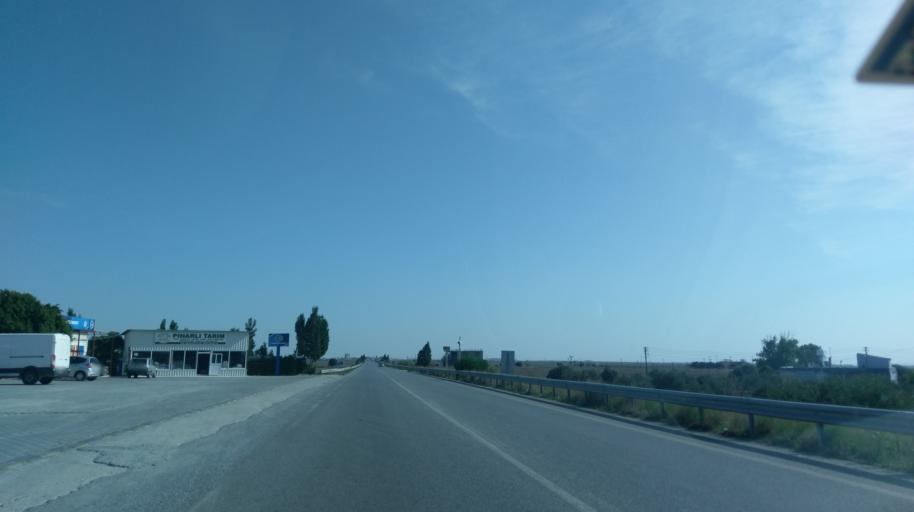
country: CY
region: Ammochostos
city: Lefkonoiko
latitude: 35.2567
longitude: 33.6872
